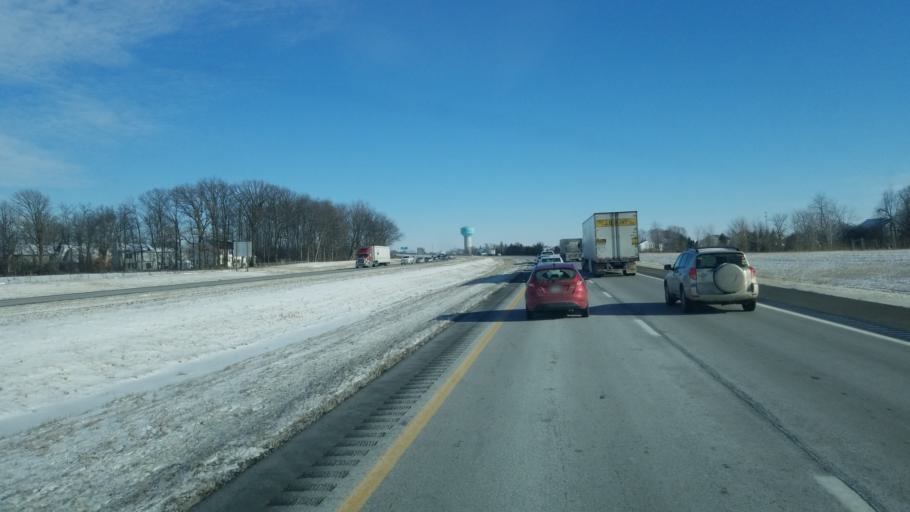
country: US
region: Ohio
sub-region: Lucas County
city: Maumee
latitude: 41.5340
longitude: -83.6677
